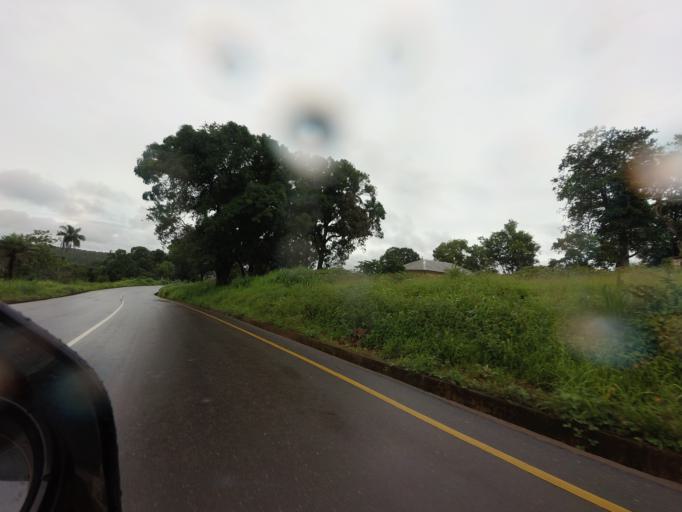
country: SL
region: Northern Province
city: Kambia
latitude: 9.1159
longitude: -12.9230
